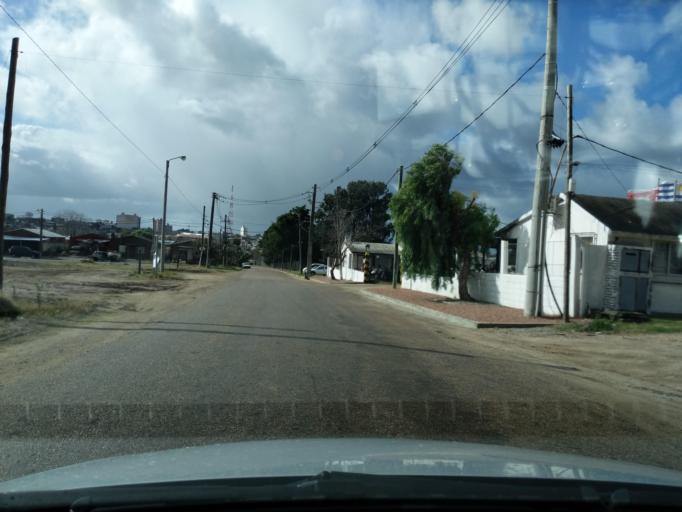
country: UY
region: Florida
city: Florida
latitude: -34.1045
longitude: -56.2269
